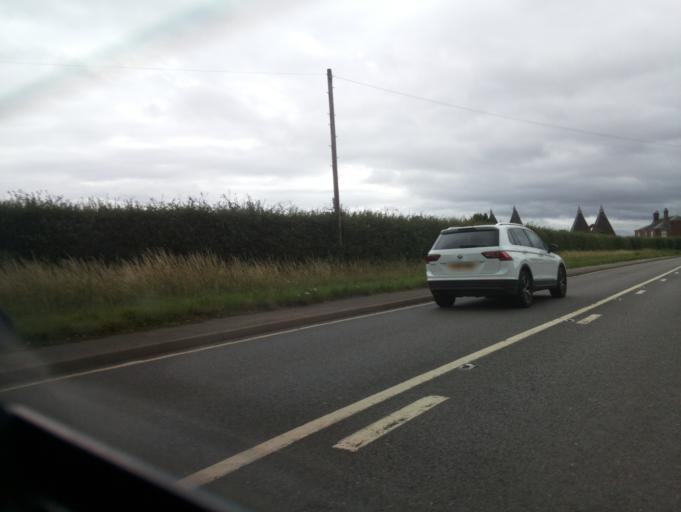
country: GB
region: England
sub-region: Worcestershire
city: Kempsey
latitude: 52.1250
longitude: -2.2184
